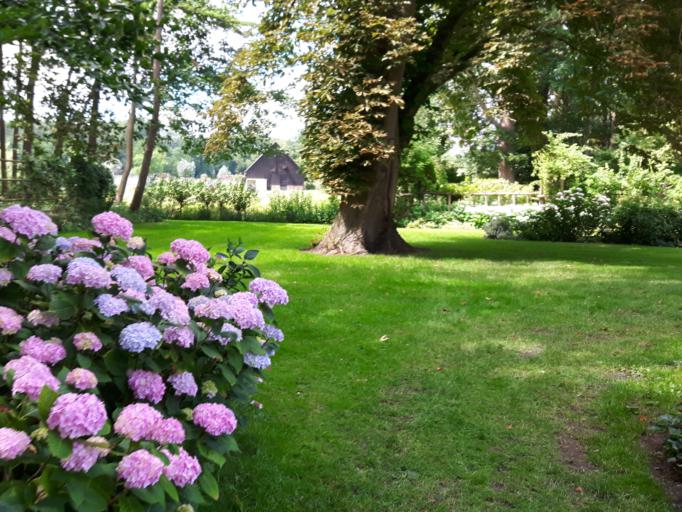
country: NL
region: Utrecht
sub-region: Gemeente Utrechtse Heuvelrug
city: Doorn
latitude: 52.0117
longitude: 5.3188
